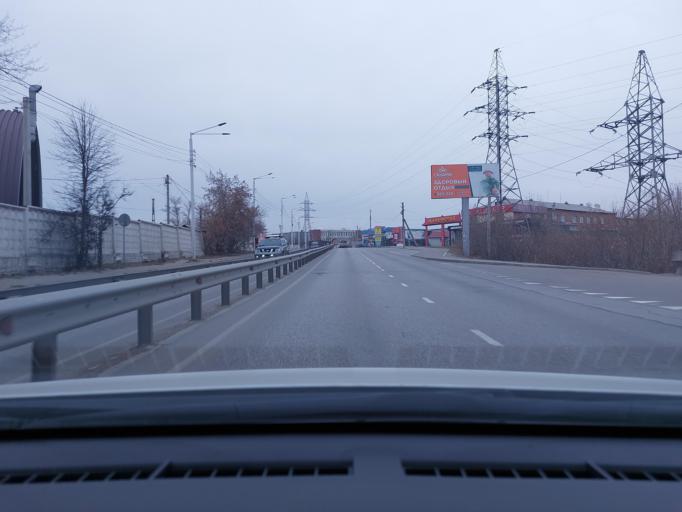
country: RU
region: Irkutsk
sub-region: Irkutskiy Rayon
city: Irkutsk
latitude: 52.3365
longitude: 104.2330
